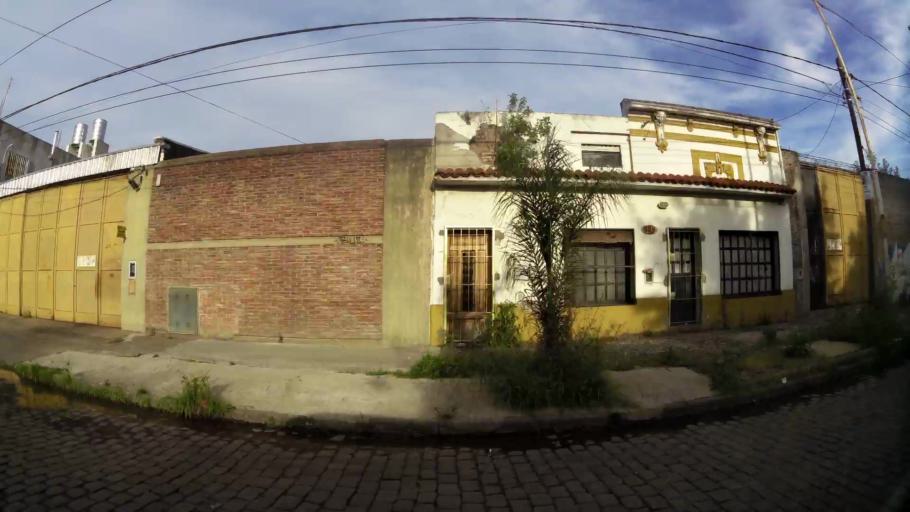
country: AR
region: Buenos Aires
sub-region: Partido de Moron
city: Moron
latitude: -34.6566
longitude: -58.6187
